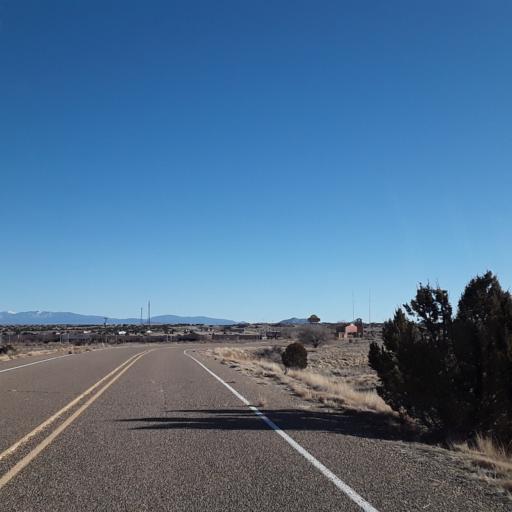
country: US
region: New Mexico
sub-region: Sandoval County
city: Santo Domingo Pueblo
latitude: 35.4526
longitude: -106.3520
